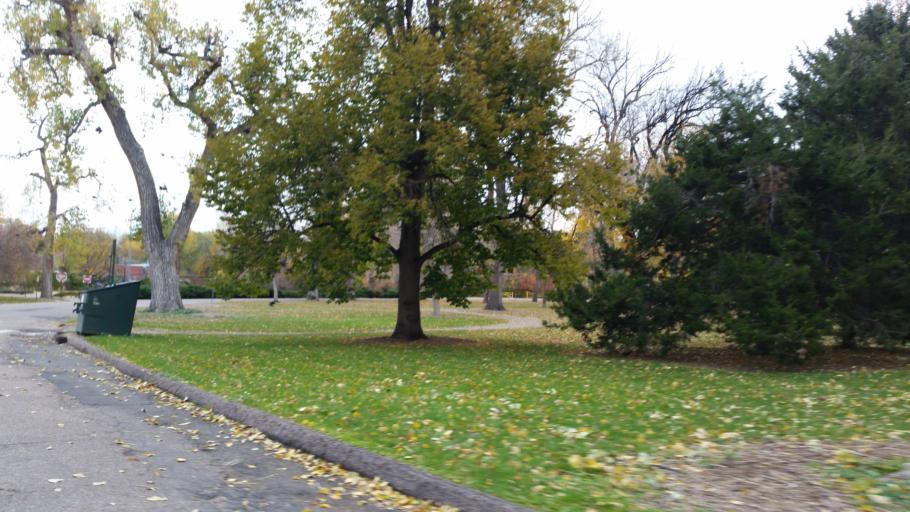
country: US
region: Colorado
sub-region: Denver County
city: Denver
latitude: 39.7488
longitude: -104.9567
